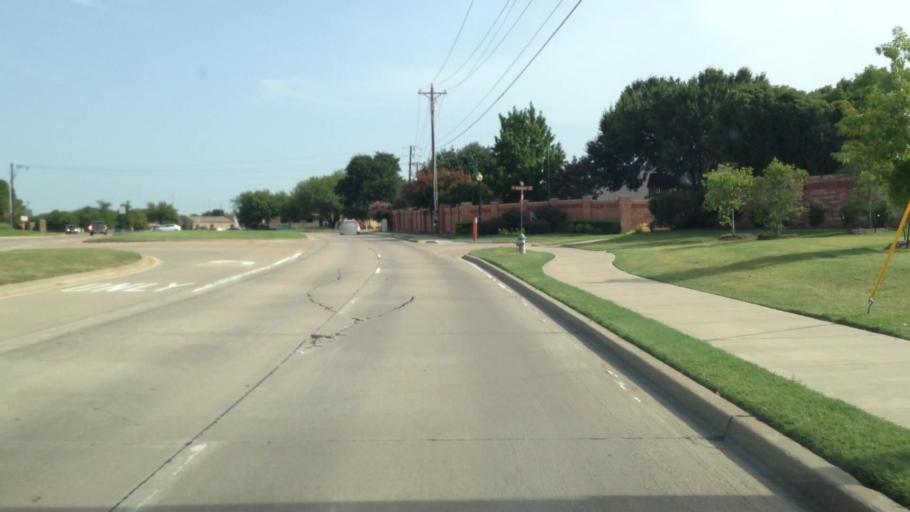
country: US
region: Texas
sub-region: Denton County
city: Flower Mound
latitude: 33.0123
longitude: -97.0448
